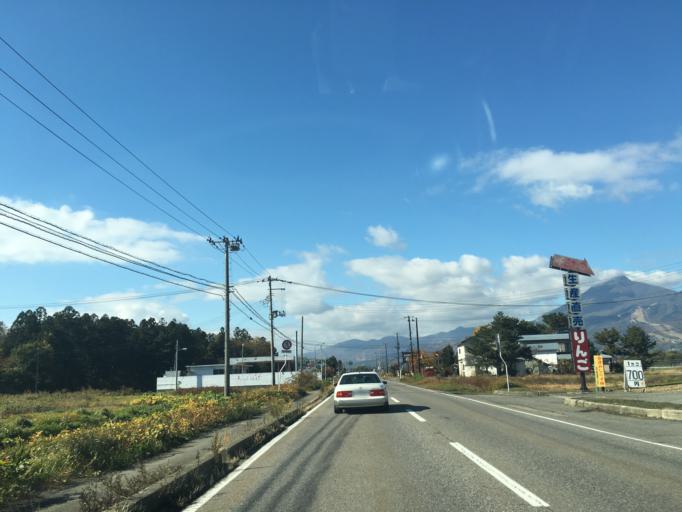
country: JP
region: Fukushima
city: Inawashiro
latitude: 37.5265
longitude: 140.1181
